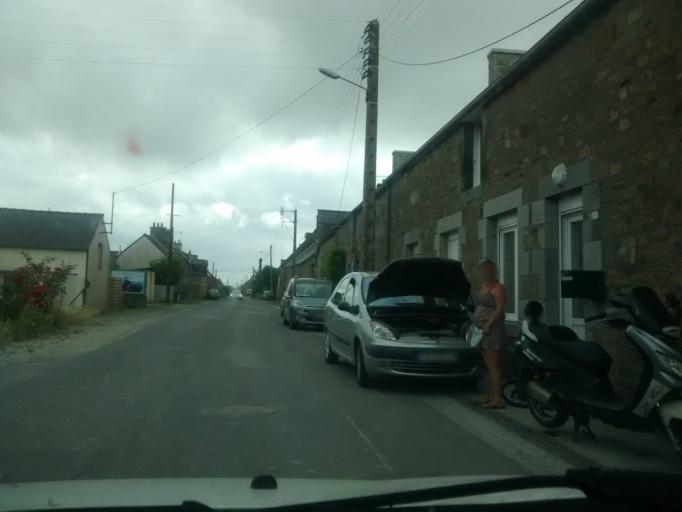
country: FR
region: Brittany
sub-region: Departement d'Ille-et-Vilaine
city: Cherrueix
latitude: 48.6083
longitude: -1.6898
